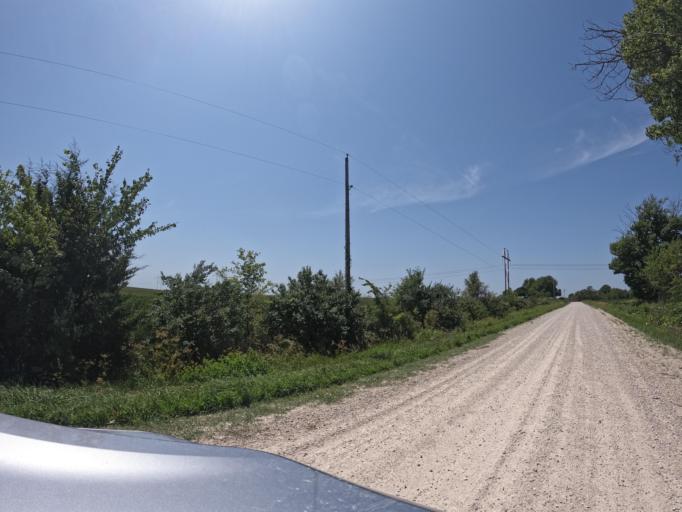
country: US
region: Iowa
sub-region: Henry County
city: Mount Pleasant
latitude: 40.9131
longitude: -91.6375
